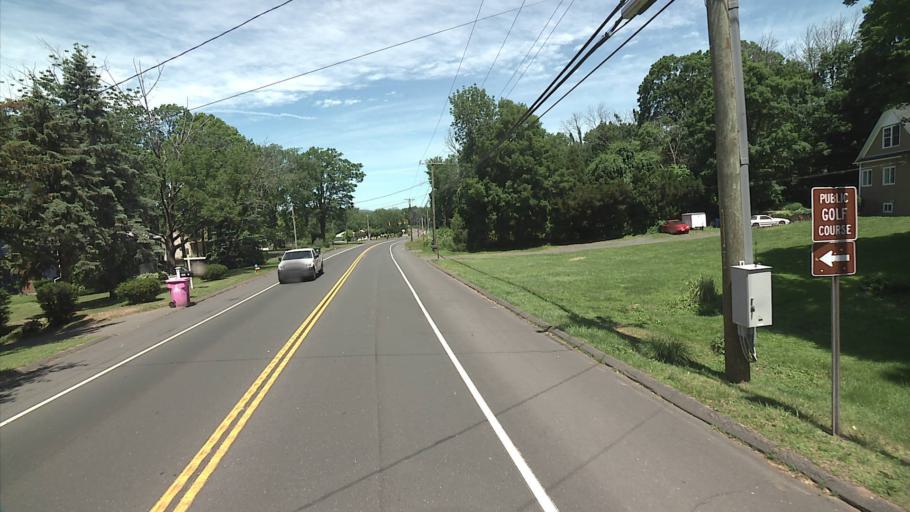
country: US
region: Connecticut
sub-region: New Haven County
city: Meriden
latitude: 41.5659
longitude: -72.8542
